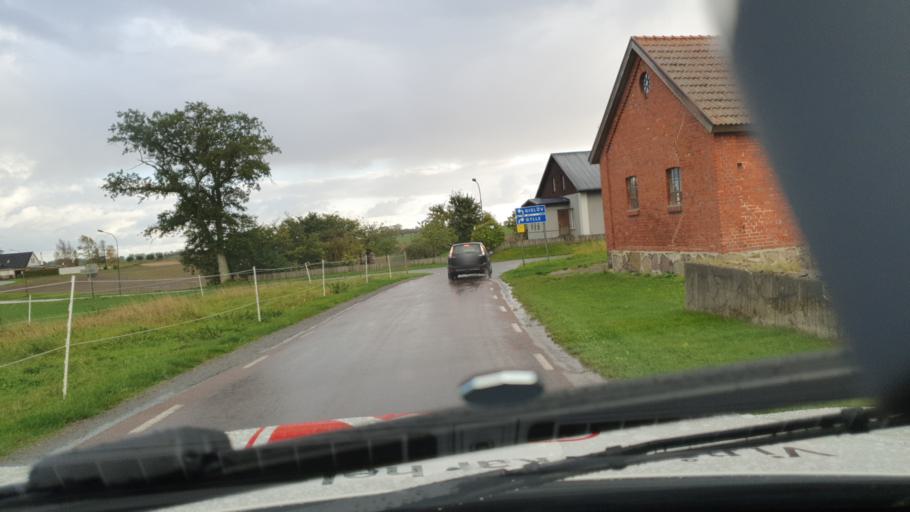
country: SE
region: Skane
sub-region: Trelleborgs Kommun
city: Trelleborg
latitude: 55.4076
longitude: 13.2102
